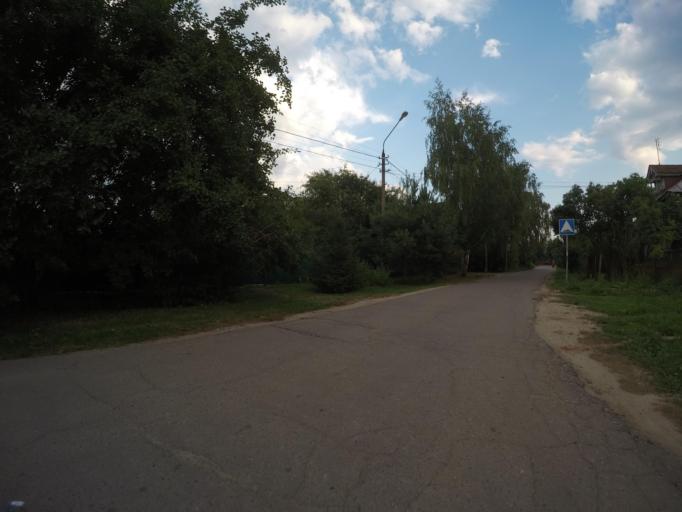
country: RU
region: Moskovskaya
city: Rechitsy
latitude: 55.6002
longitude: 38.5125
